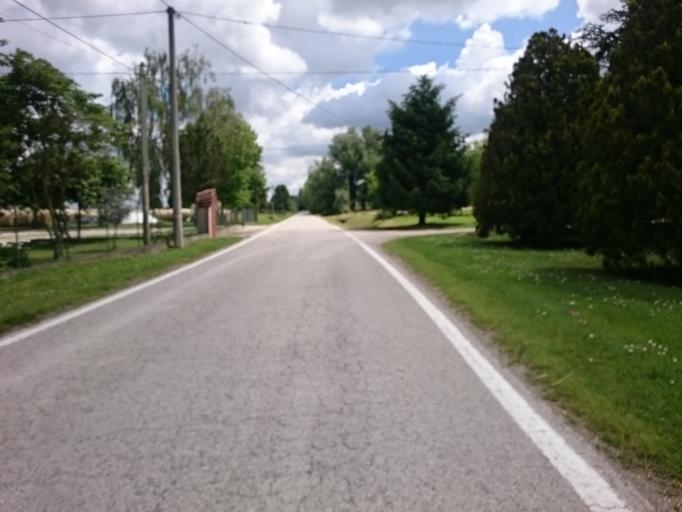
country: IT
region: Veneto
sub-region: Provincia di Padova
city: Piazzola sul Brenta
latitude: 45.5241
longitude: 11.7696
